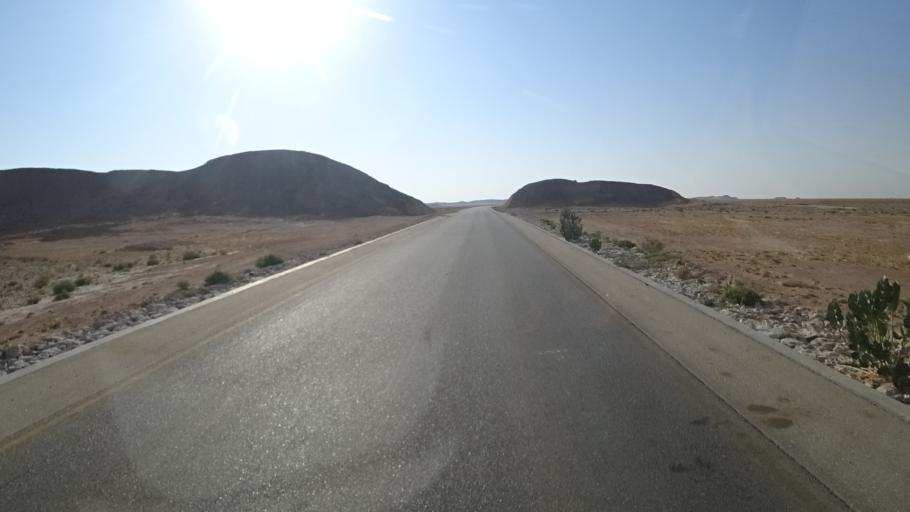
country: OM
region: Zufar
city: Salalah
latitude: 17.6393
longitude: 53.8913
